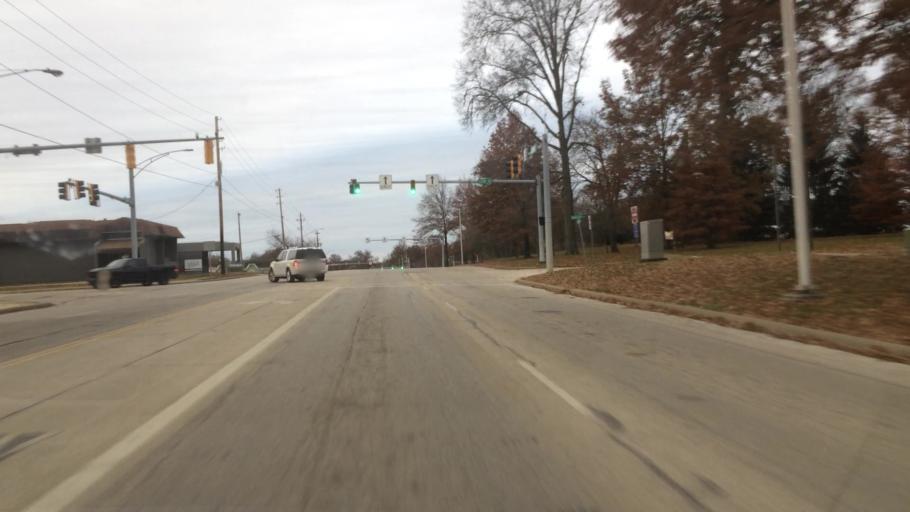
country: US
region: Ohio
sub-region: Summit County
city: Stow
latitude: 41.1694
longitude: -81.4404
